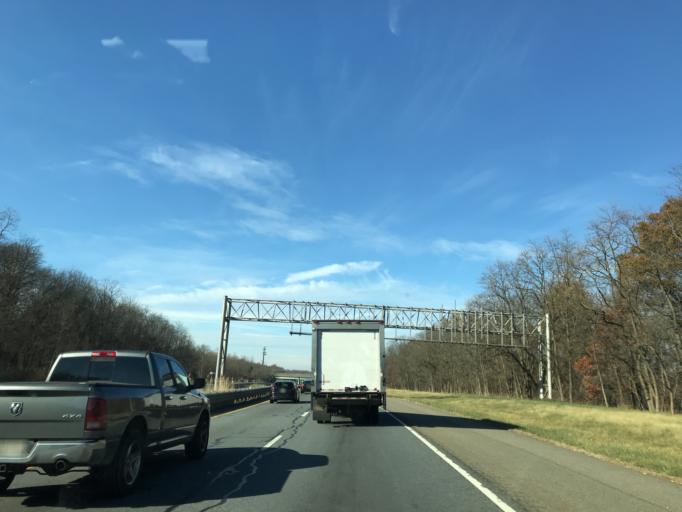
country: US
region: New Jersey
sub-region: Morris County
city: Chatham
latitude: 40.7517
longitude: -74.3751
